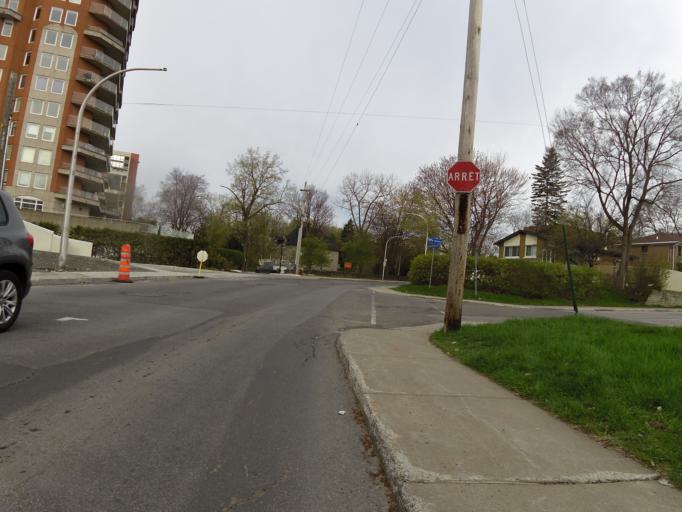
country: CA
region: Quebec
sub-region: Laval
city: Laval
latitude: 45.5397
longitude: -73.7227
